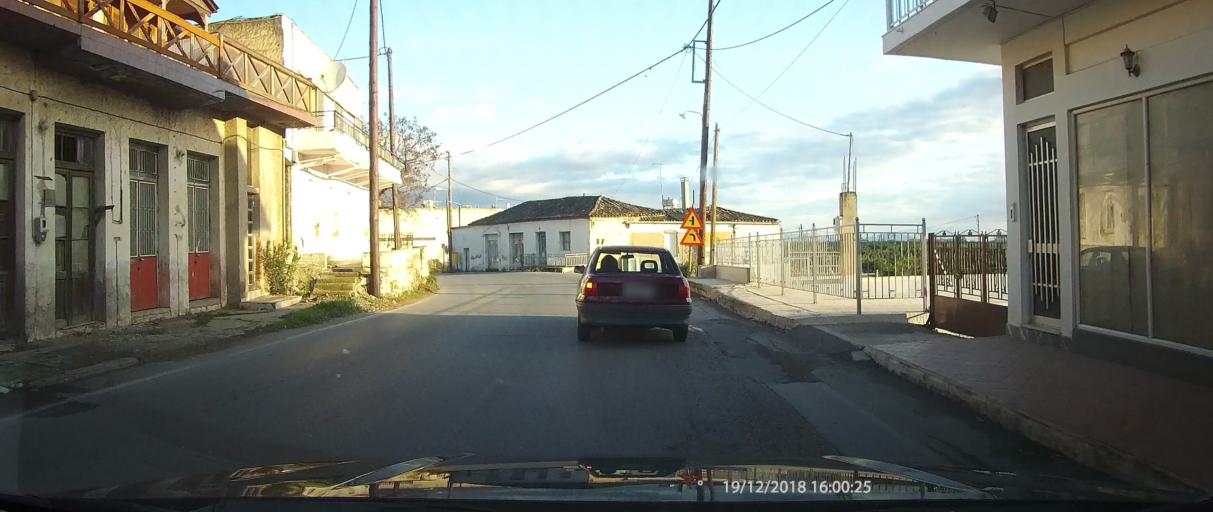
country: GR
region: Peloponnese
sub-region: Nomos Lakonias
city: Skala
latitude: 36.8547
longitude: 22.6779
